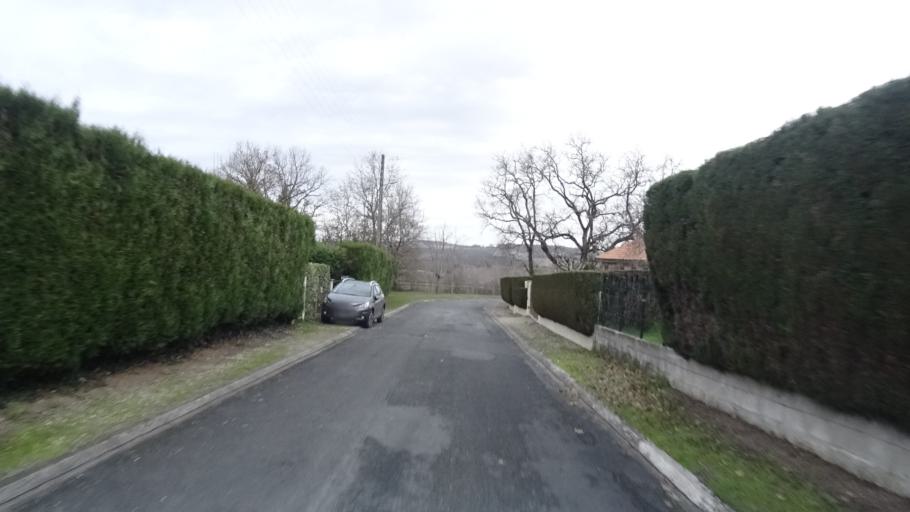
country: FR
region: Aquitaine
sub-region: Departement de la Dordogne
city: Saint-Aulaye
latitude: 45.2037
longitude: 0.1304
